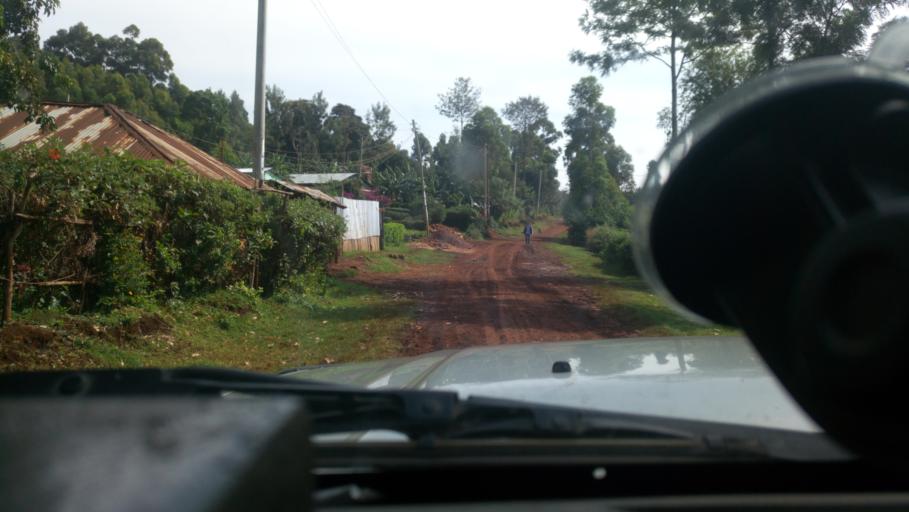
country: KE
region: Nyamira District
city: Nyamira
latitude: -0.5688
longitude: 34.9403
